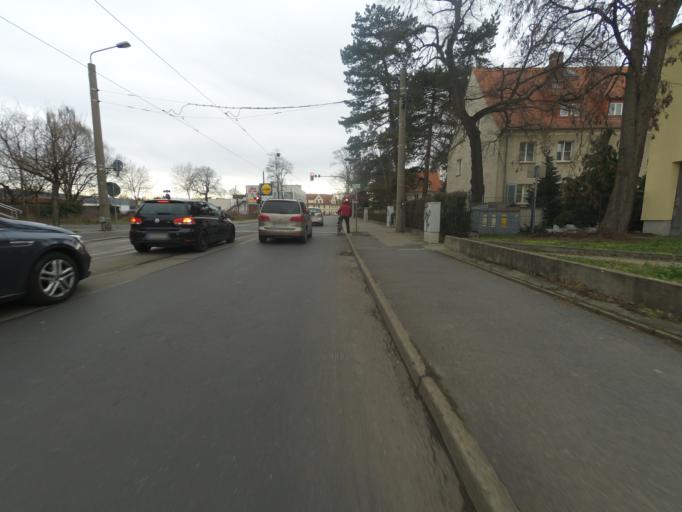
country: DE
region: Saxony
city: Heidenau
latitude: 51.0294
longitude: 13.8328
